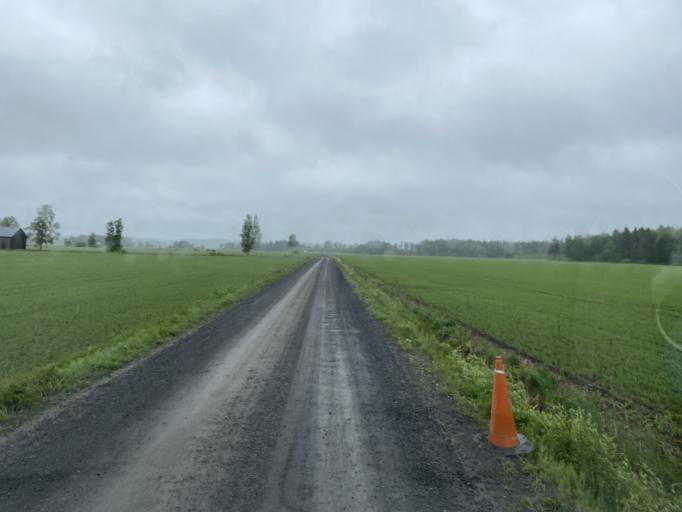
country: FI
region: Haeme
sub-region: Forssa
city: Forssa
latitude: 60.9458
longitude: 23.5925
